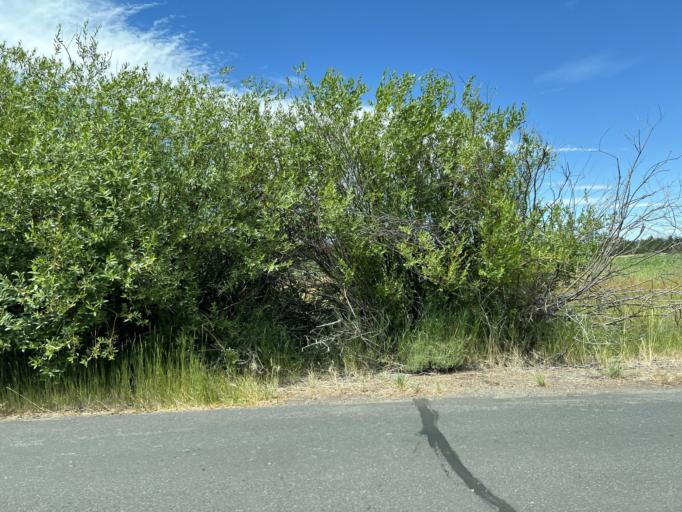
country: US
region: Oregon
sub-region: Deschutes County
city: Sunriver
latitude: 43.8851
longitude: -121.4511
